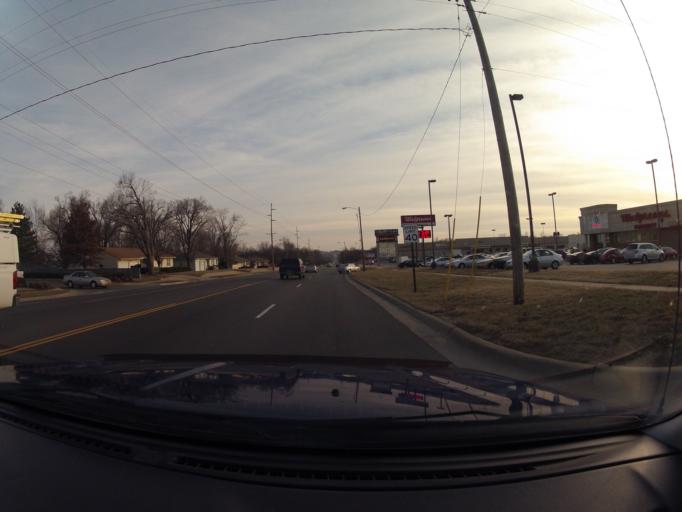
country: US
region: Kansas
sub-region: Shawnee County
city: Topeka
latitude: 39.0286
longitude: -95.7437
